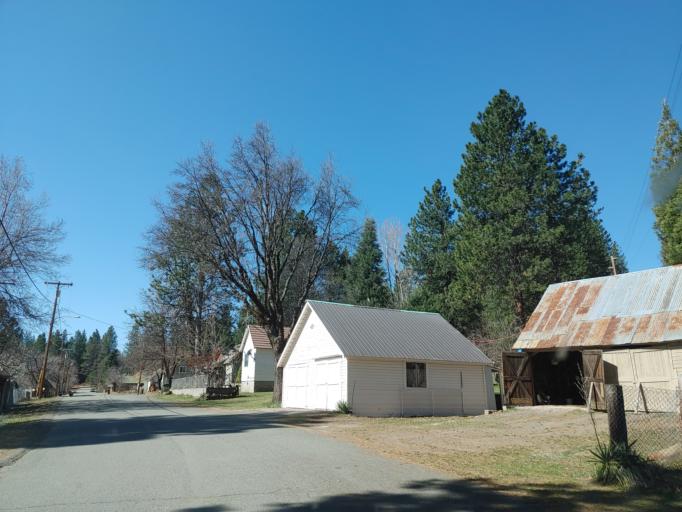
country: US
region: California
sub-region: Siskiyou County
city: McCloud
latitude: 41.2625
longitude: -122.1409
